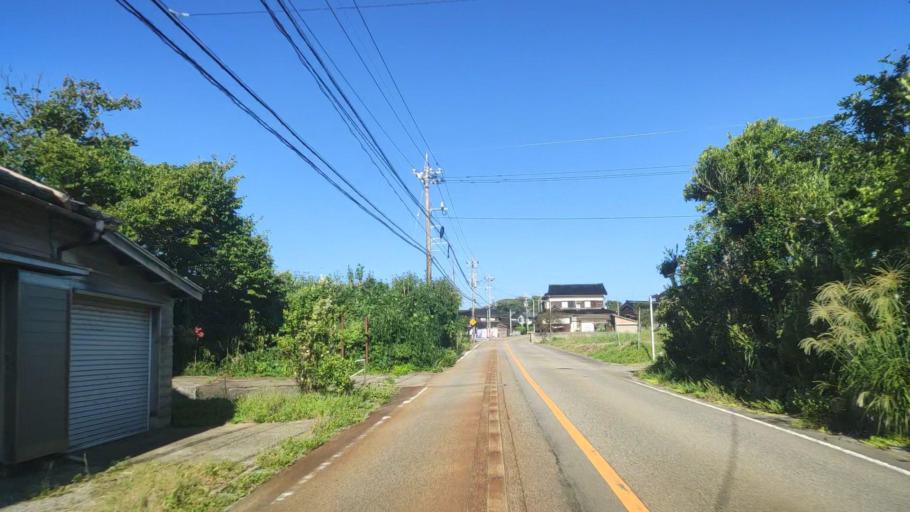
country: JP
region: Ishikawa
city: Hakui
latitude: 36.9255
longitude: 136.7617
